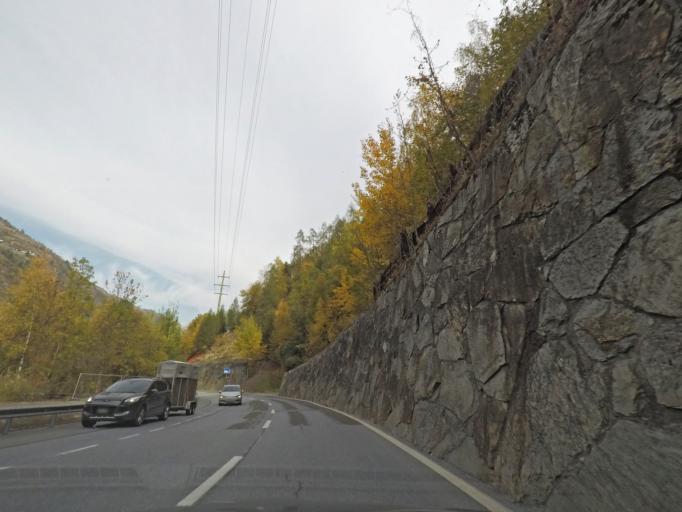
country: CH
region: Valais
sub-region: Visp District
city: Grachen
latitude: 46.2059
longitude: 7.8304
